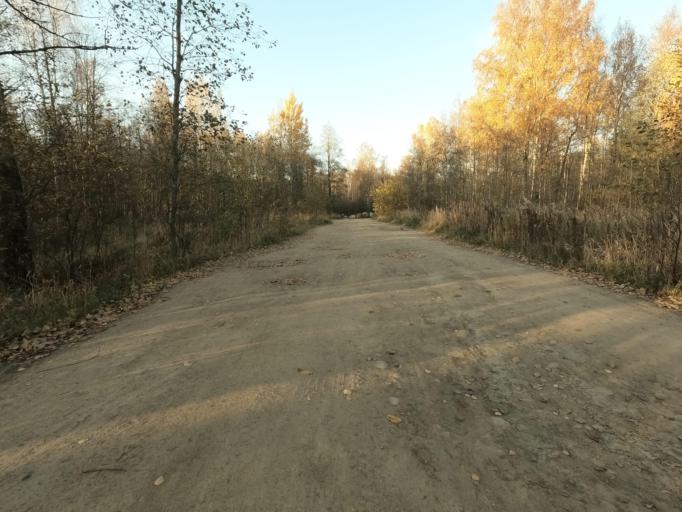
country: RU
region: Leningrad
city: Sinyavino
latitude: 59.8769
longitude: 31.0403
